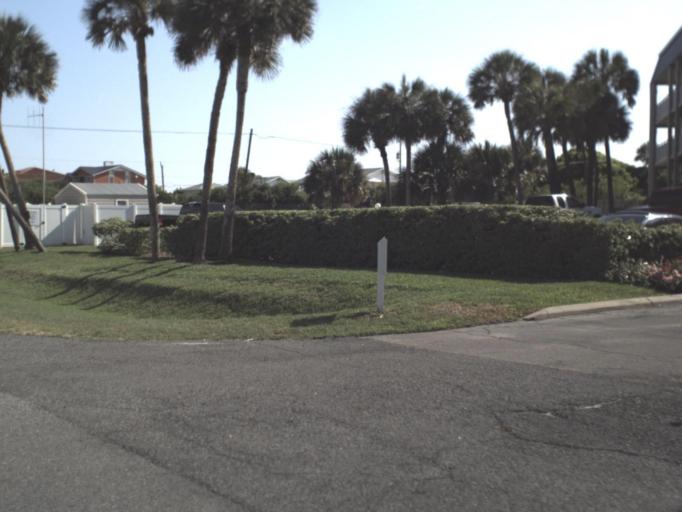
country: US
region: Florida
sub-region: Saint Johns County
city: Butler Beach
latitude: 29.7448
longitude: -81.2446
